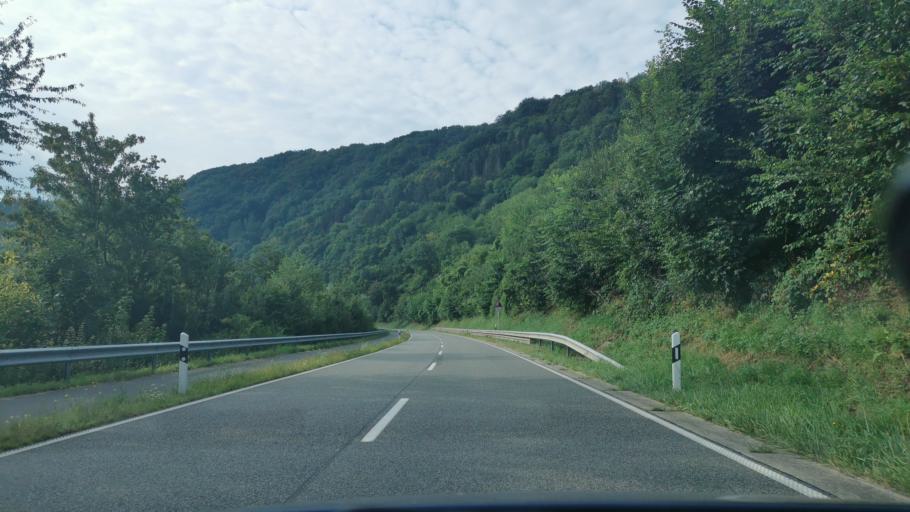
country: DE
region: Rheinland-Pfalz
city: Minheim
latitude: 49.8661
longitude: 6.9255
